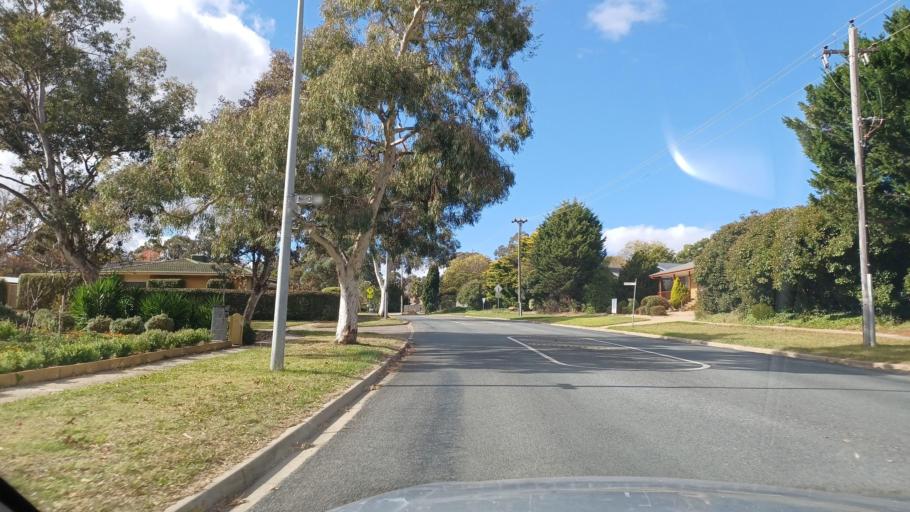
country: AU
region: Australian Capital Territory
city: Belconnen
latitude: -35.2073
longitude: 149.0668
